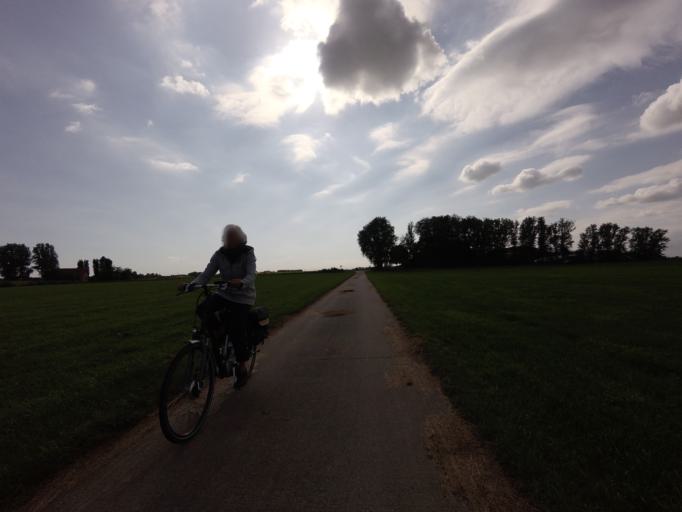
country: NL
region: Friesland
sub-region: Gemeente Littenseradiel
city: Makkum
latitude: 53.0864
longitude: 5.6323
